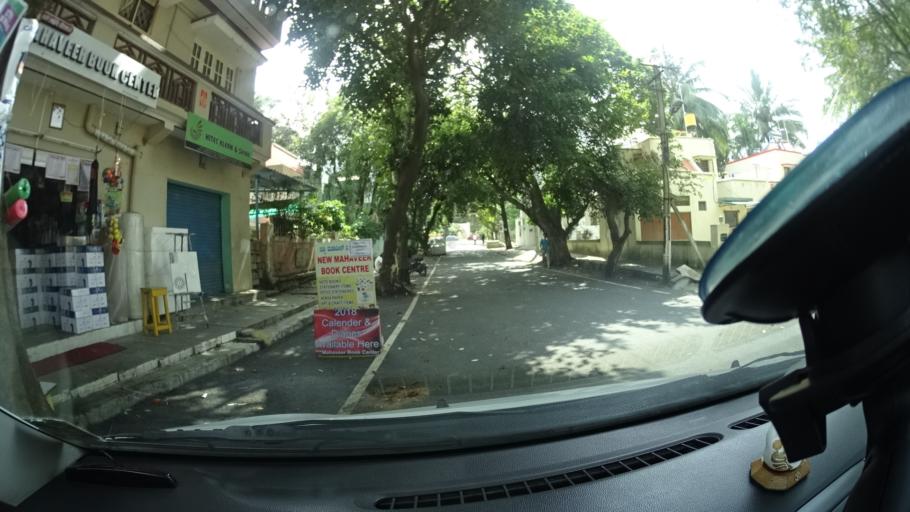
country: IN
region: Karnataka
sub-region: Bangalore Urban
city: Yelahanka
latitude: 13.1024
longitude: 77.5732
